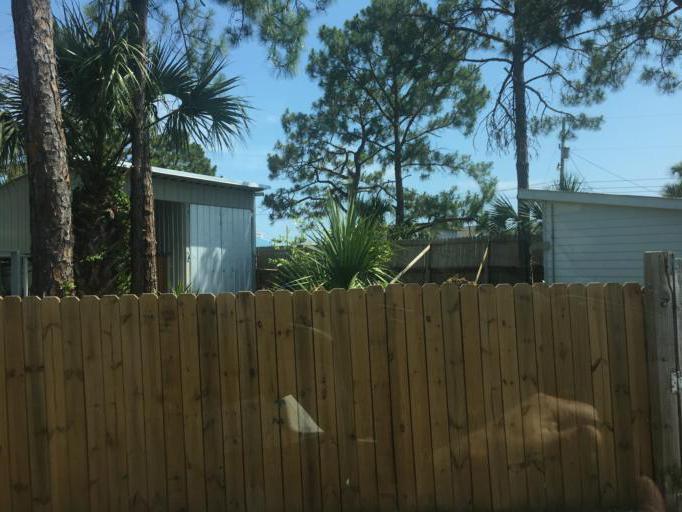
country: US
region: Florida
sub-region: Bay County
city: Lower Grand Lagoon
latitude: 30.1620
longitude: -85.7768
